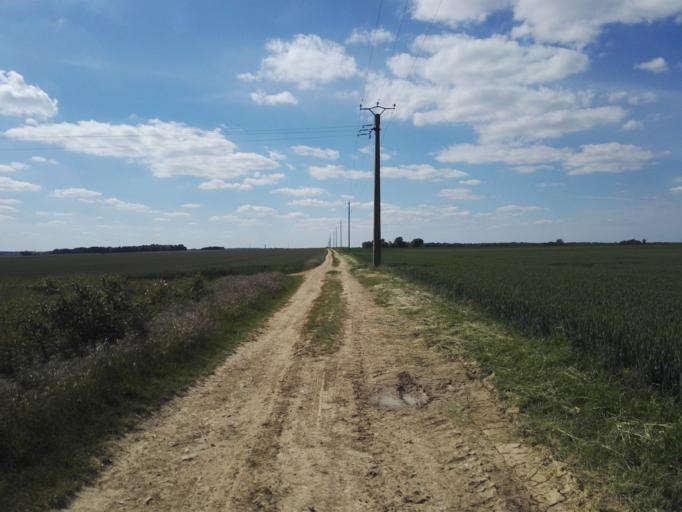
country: FR
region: Haute-Normandie
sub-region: Departement de l'Eure
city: Pacy-sur-Eure
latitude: 48.9937
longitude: 1.3587
